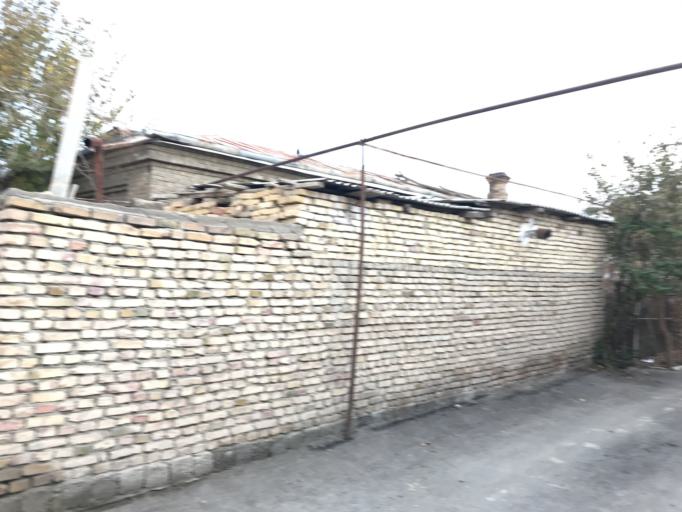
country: UZ
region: Bukhara
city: Kogon
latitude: 39.7191
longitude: 64.5474
